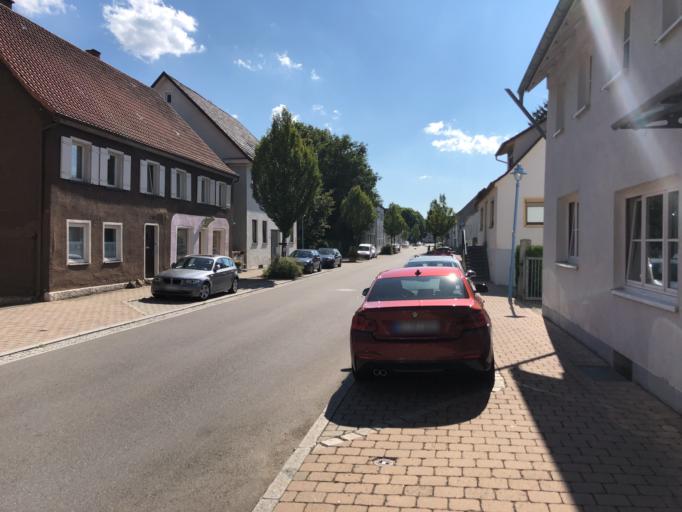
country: DE
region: Baden-Wuerttemberg
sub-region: Tuebingen Region
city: Bad Buchau
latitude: 48.0628
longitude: 9.6072
